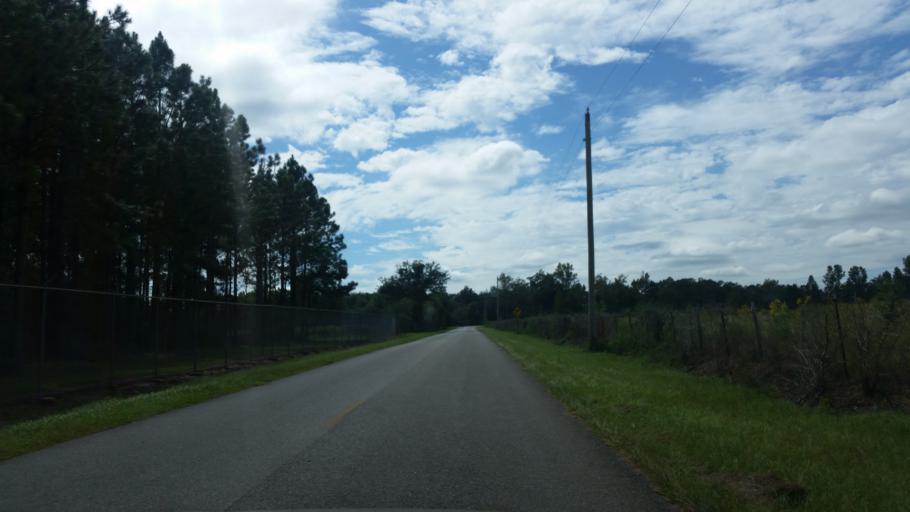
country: US
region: Florida
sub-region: Santa Rosa County
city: Point Baker
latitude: 30.7350
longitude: -87.0365
